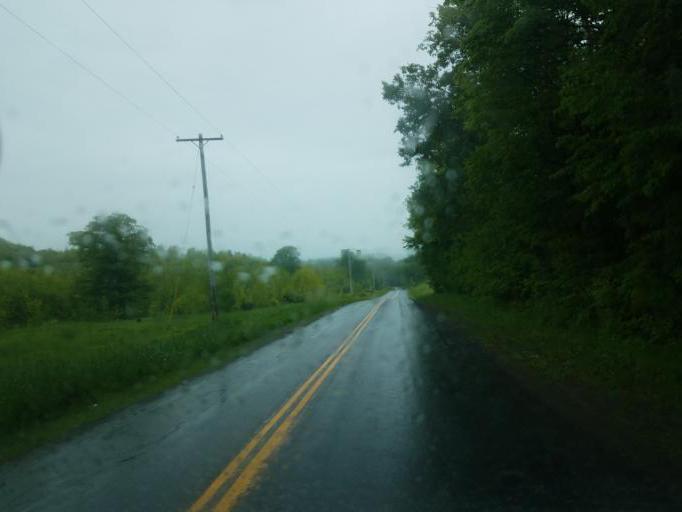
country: US
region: New York
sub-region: Herkimer County
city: Ilion
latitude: 42.9471
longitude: -75.0295
